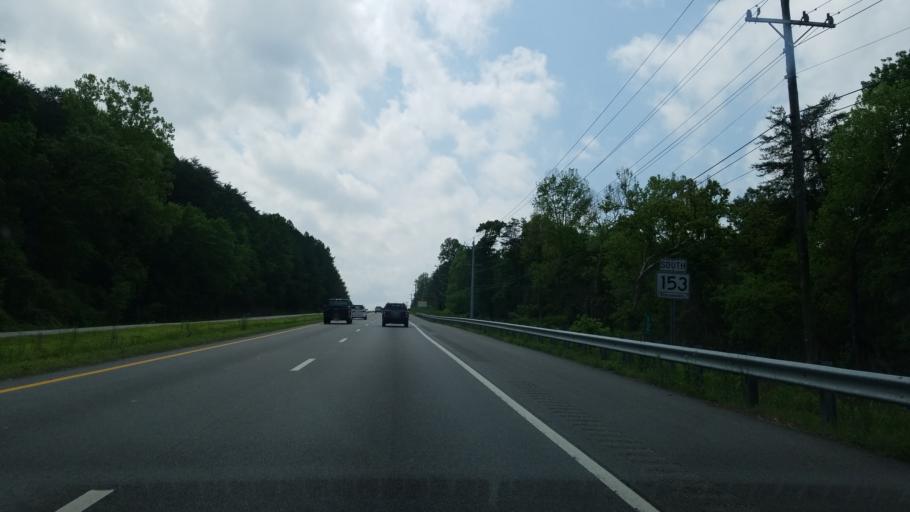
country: US
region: Tennessee
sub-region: Hamilton County
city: Falling Water
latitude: 35.1760
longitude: -85.2473
